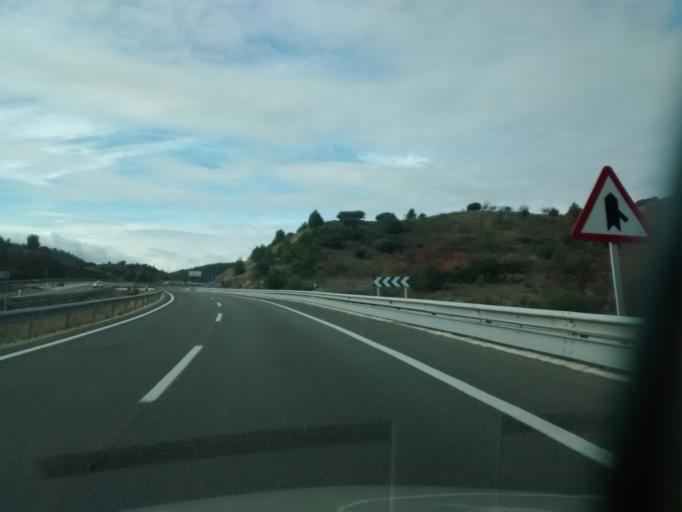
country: ES
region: Aragon
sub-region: Provincia de Zaragoza
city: Bubierca
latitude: 41.3235
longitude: -1.8648
